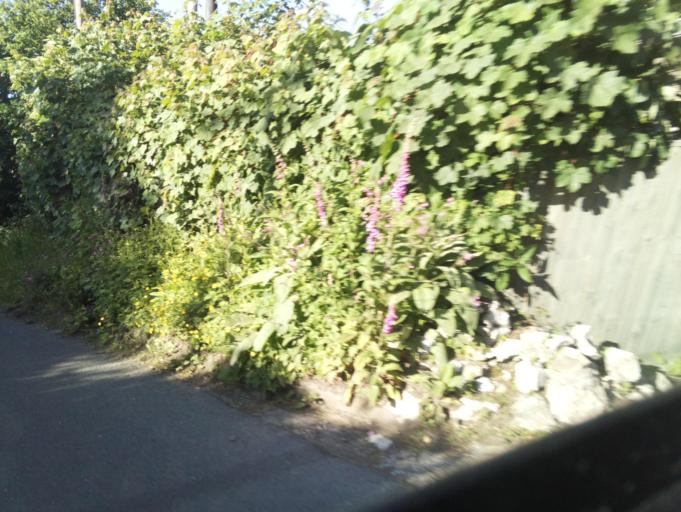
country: GB
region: England
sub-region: Somerset
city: Crewkerne
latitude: 50.8236
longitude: -2.8580
